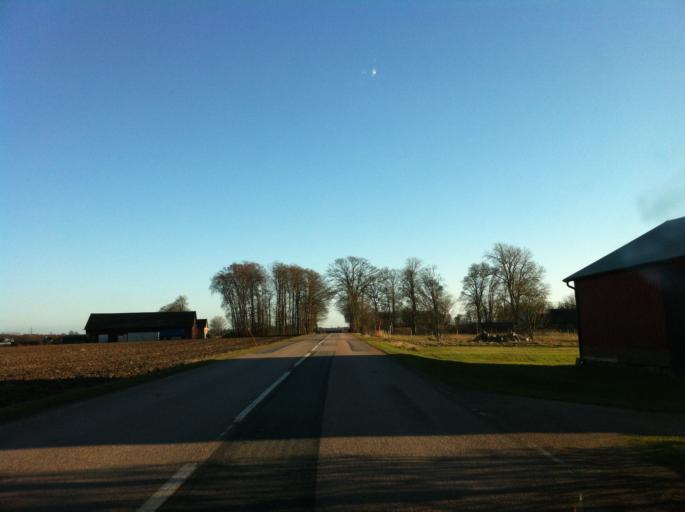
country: SE
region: Skane
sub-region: Helsingborg
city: Morarp
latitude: 56.0221
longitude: 12.9050
